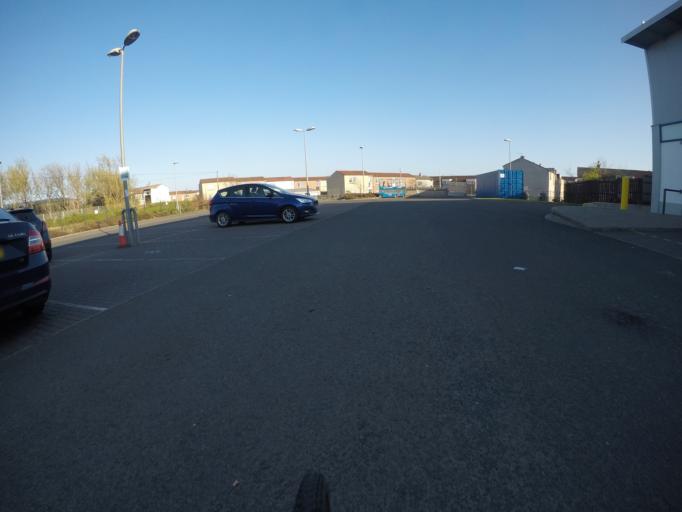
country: GB
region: Scotland
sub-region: North Ayrshire
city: Stevenston
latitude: 55.6387
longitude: -4.7614
